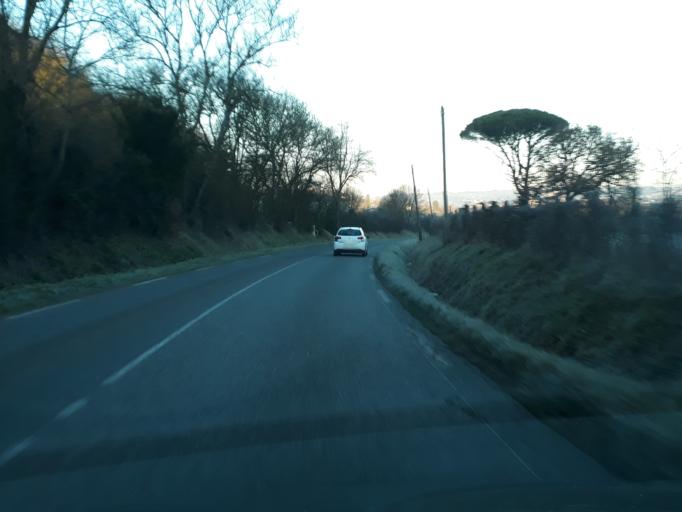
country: FR
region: Midi-Pyrenees
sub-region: Departement du Gers
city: Pavie
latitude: 43.6299
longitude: 0.6167
